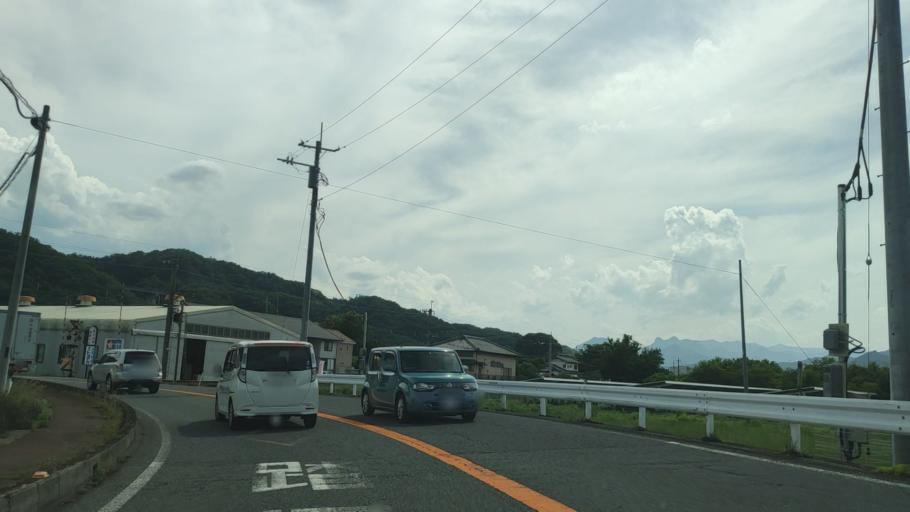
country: JP
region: Gunma
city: Tomioka
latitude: 36.2439
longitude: 138.8512
